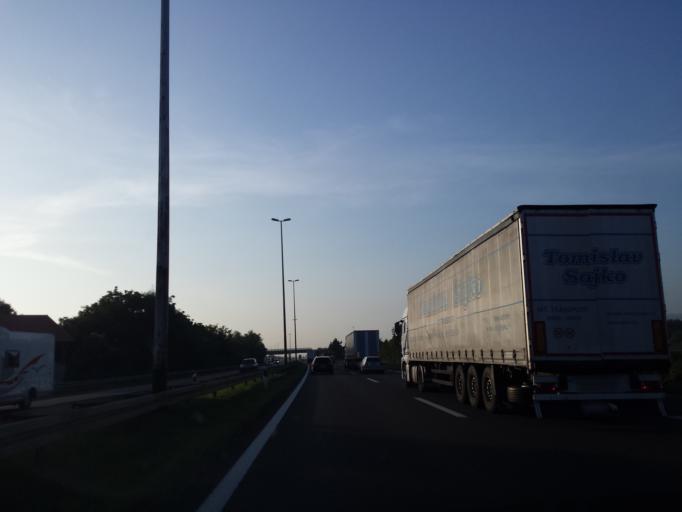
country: HR
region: Grad Zagreb
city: Lucko
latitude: 45.7666
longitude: 15.8919
